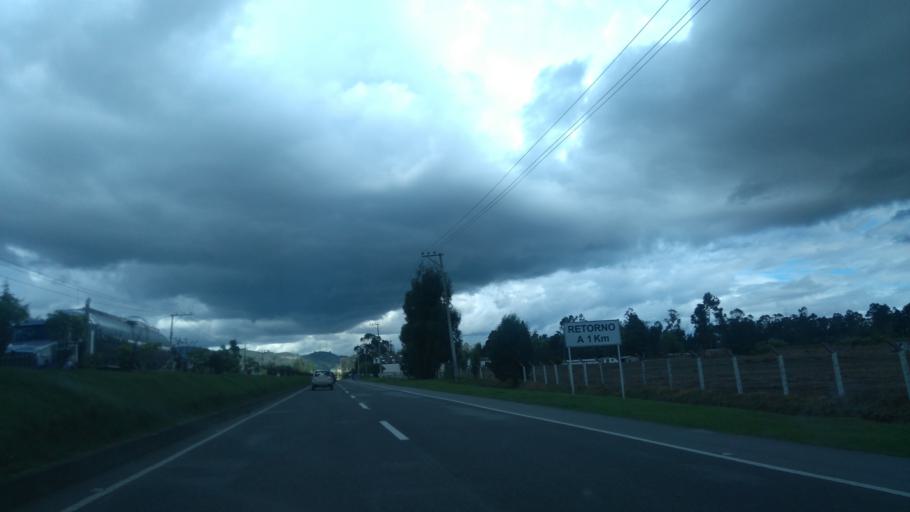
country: CO
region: Cundinamarca
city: El Rosal
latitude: 4.8276
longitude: -74.2408
